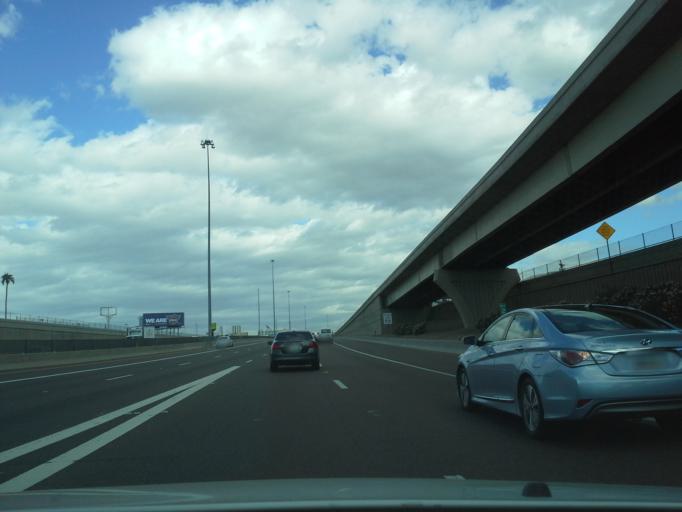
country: US
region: Arizona
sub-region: Maricopa County
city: Phoenix
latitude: 33.4669
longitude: -112.1102
